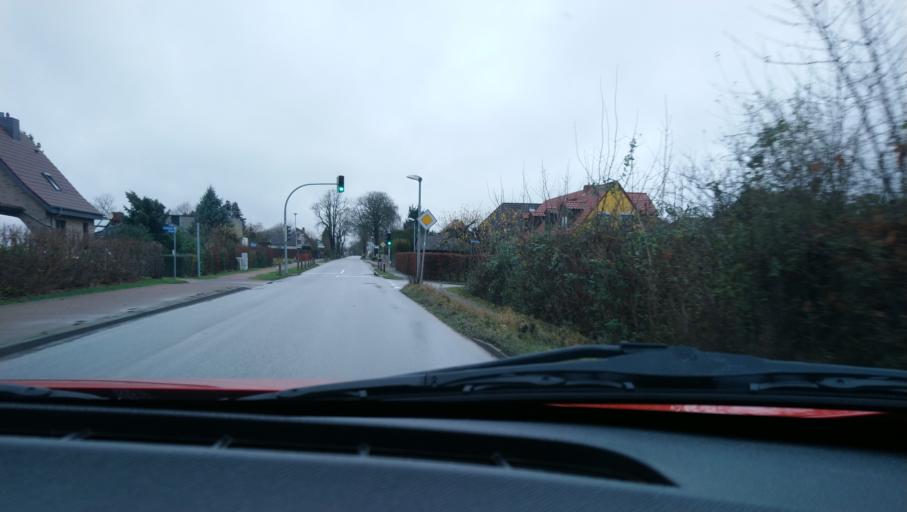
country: DE
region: Mecklenburg-Vorpommern
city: Seehof
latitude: 53.6927
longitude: 11.4312
